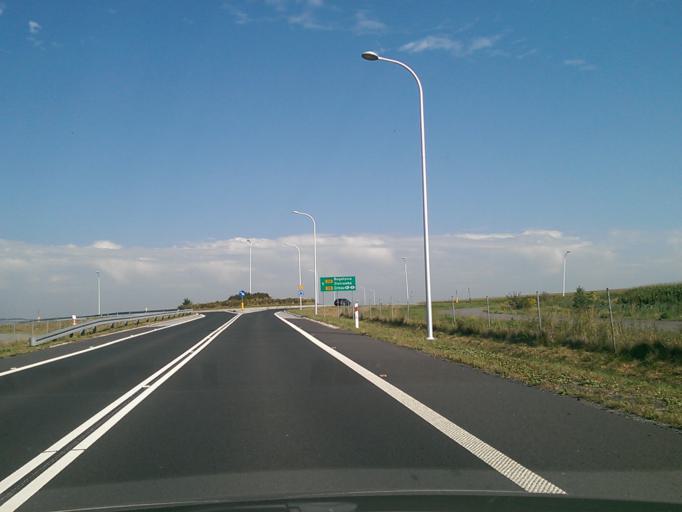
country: CZ
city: Hradek nad Nisou
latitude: 50.8733
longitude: 14.8448
